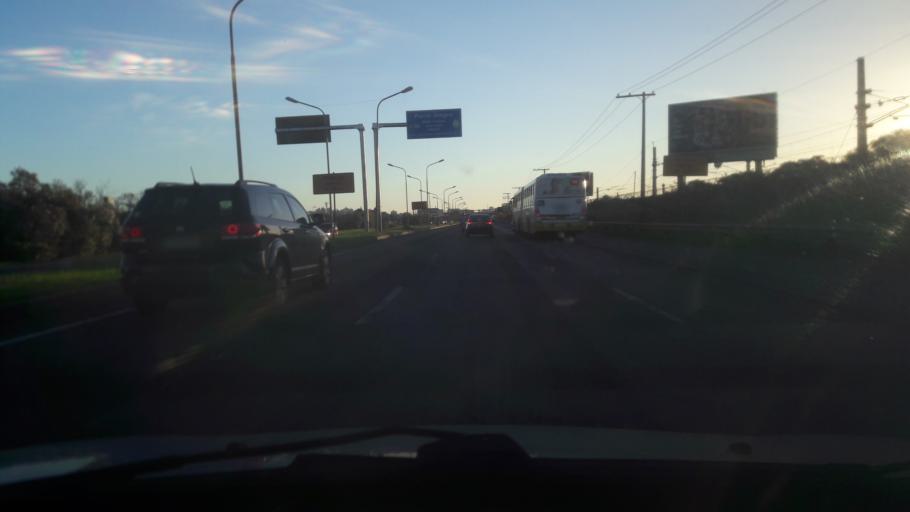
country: BR
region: Rio Grande do Sul
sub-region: Porto Alegre
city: Porto Alegre
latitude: -29.9915
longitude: -51.1852
